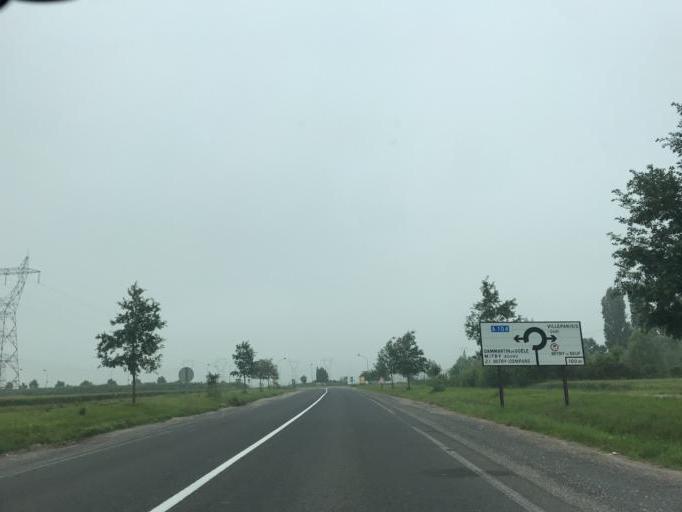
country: FR
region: Ile-de-France
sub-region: Departement de Seine-et-Marne
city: Mitry-Mory
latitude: 48.9647
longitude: 2.6020
